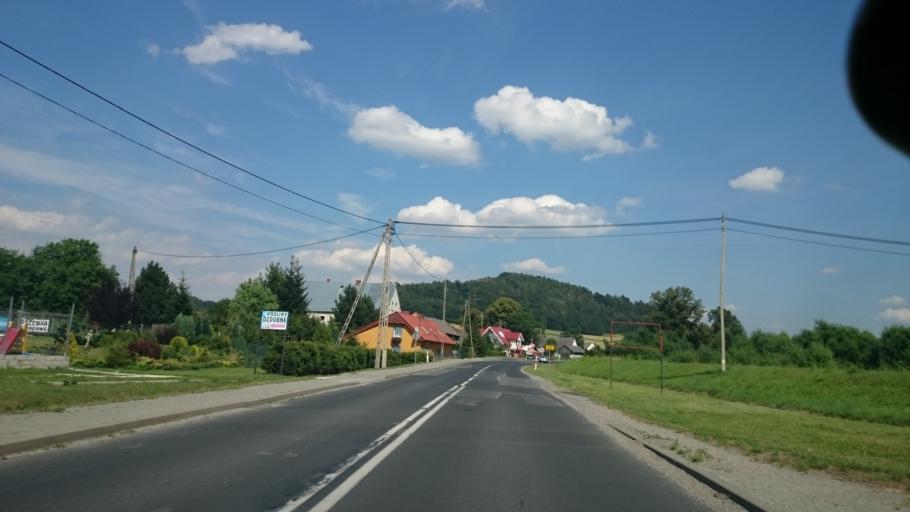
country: PL
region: Lower Silesian Voivodeship
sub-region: Powiat klodzki
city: Bystrzyca Klodzka
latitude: 50.3550
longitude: 16.7327
